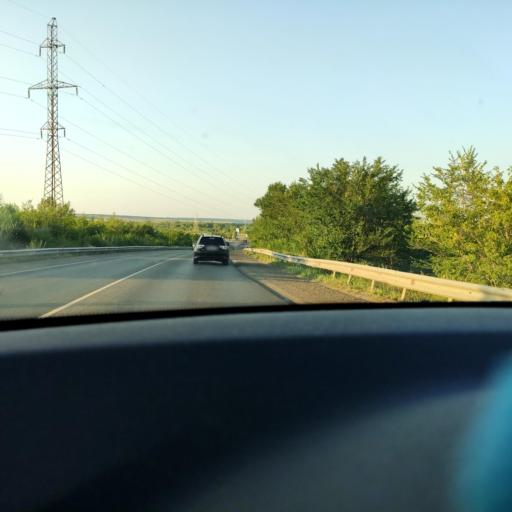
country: RU
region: Samara
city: Kinel'
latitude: 53.2434
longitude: 50.5832
